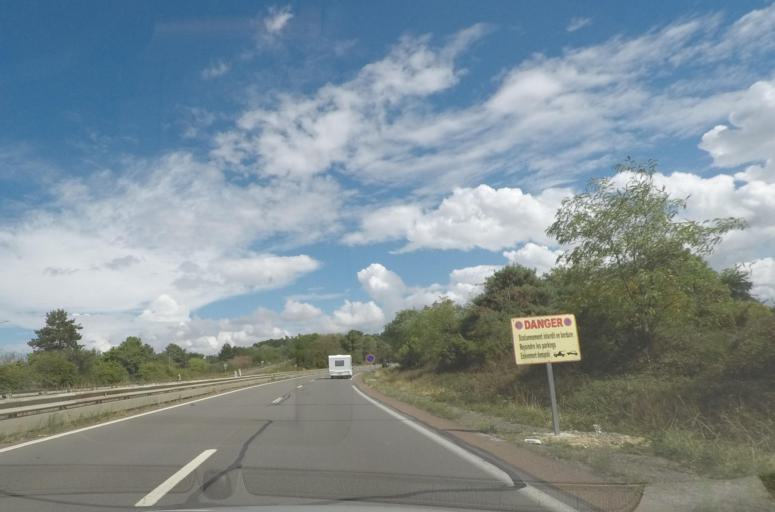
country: FR
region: Pays de la Loire
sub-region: Departement de la Sarthe
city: Arnage
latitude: 47.9540
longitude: 0.1973
